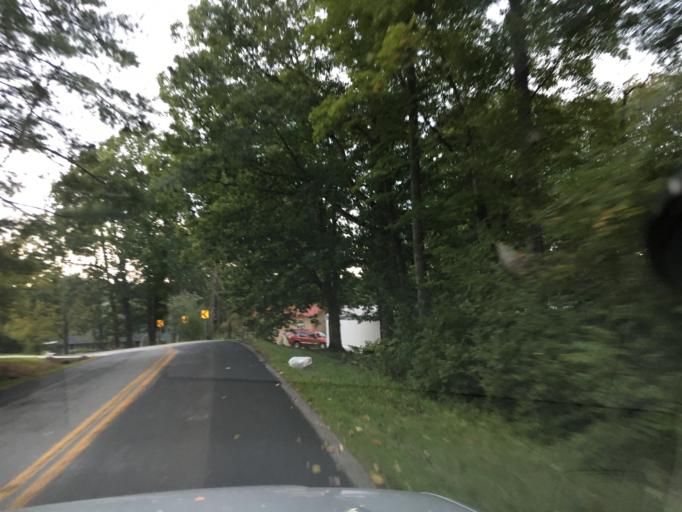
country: US
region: North Carolina
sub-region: McDowell County
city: Marion
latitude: 35.6995
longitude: -81.9145
